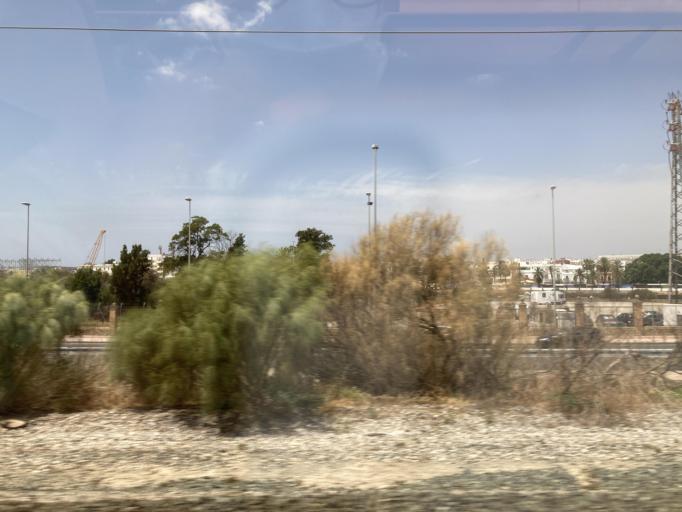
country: ES
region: Andalusia
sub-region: Provincia de Cadiz
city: El Puerto de Santa Maria
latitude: 36.5980
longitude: -6.2202
